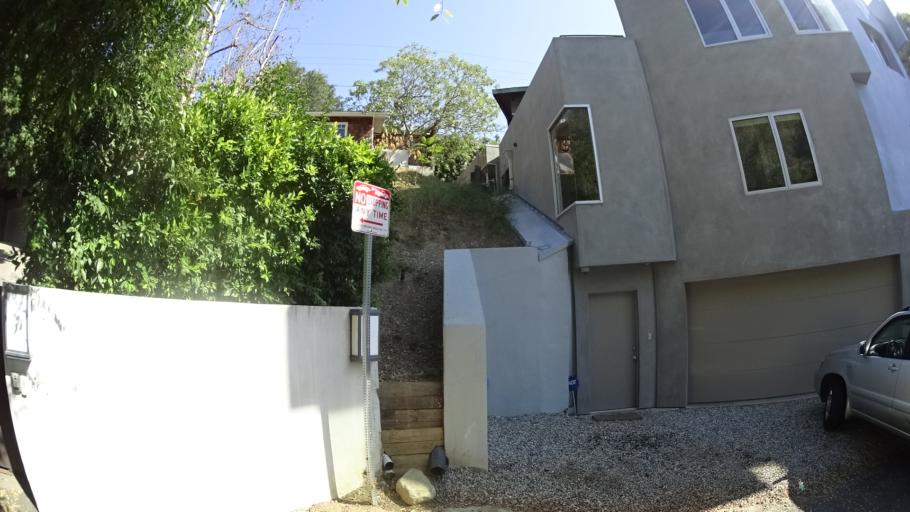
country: US
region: California
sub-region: Los Angeles County
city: Universal City
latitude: 34.1394
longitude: -118.3741
